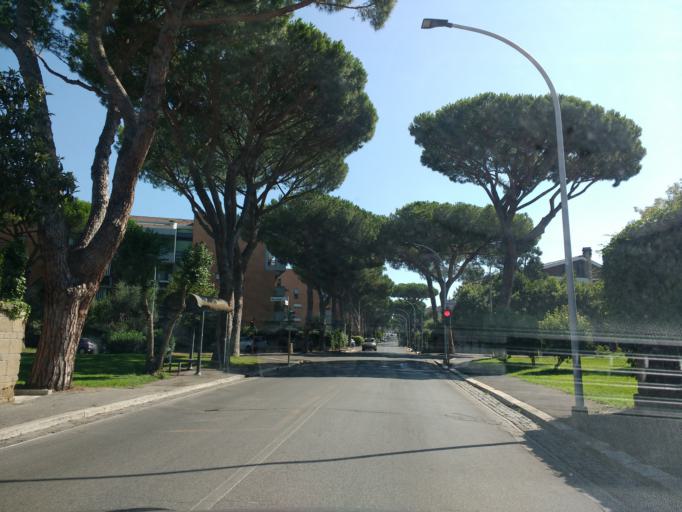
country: IT
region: Latium
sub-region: Citta metropolitana di Roma Capitale
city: Acilia-Castel Fusano-Ostia Antica
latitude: 41.7673
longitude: 12.3666
